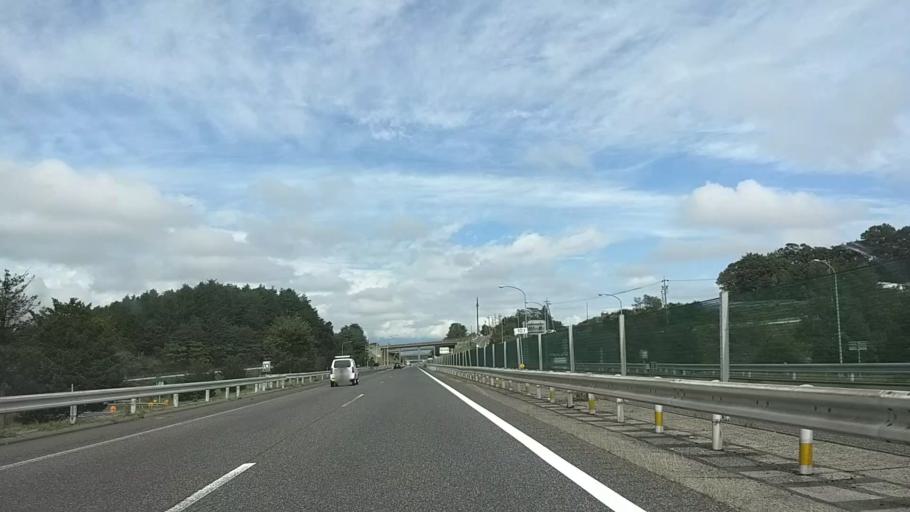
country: JP
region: Nagano
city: Shiojiri
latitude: 36.1167
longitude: 137.9826
